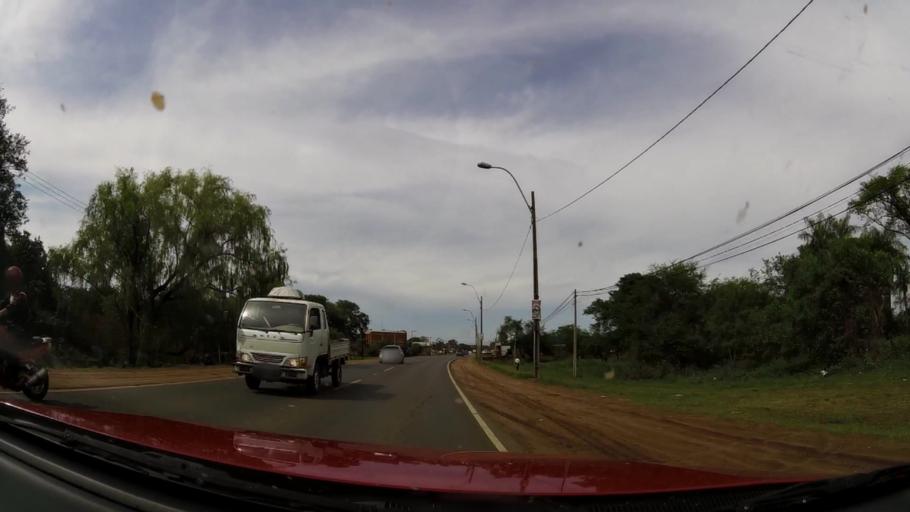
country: PY
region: Central
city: Limpio
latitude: -25.1569
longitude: -57.4740
